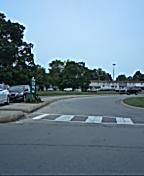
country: US
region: Kentucky
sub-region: Jefferson County
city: Middletown
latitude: 38.2463
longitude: -85.5262
